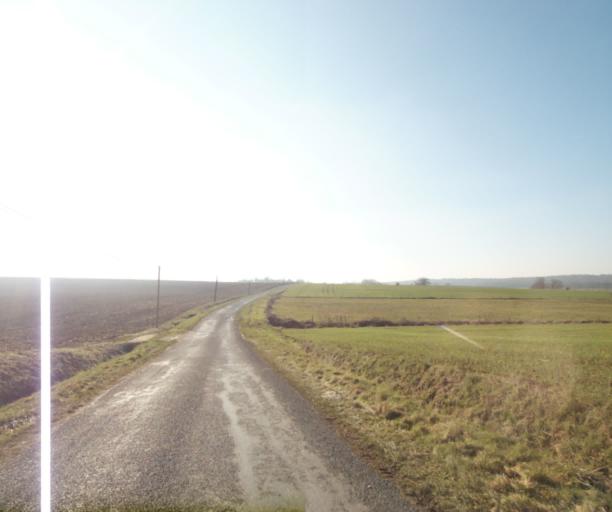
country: FR
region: Champagne-Ardenne
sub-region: Departement de la Haute-Marne
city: Bienville
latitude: 48.5315
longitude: 5.0070
